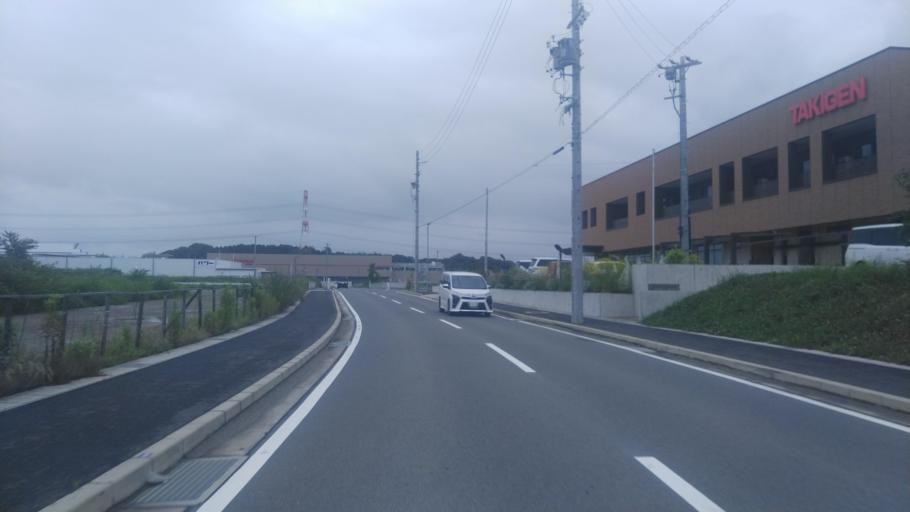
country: JP
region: Aichi
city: Kasugai
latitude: 35.2552
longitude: 137.0296
